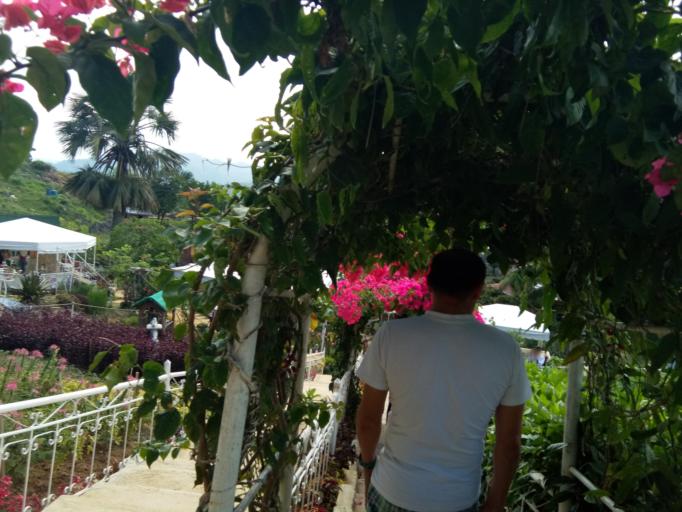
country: PH
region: Central Visayas
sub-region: Province of Cebu
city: Cebu City
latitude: 10.4068
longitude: 123.8667
